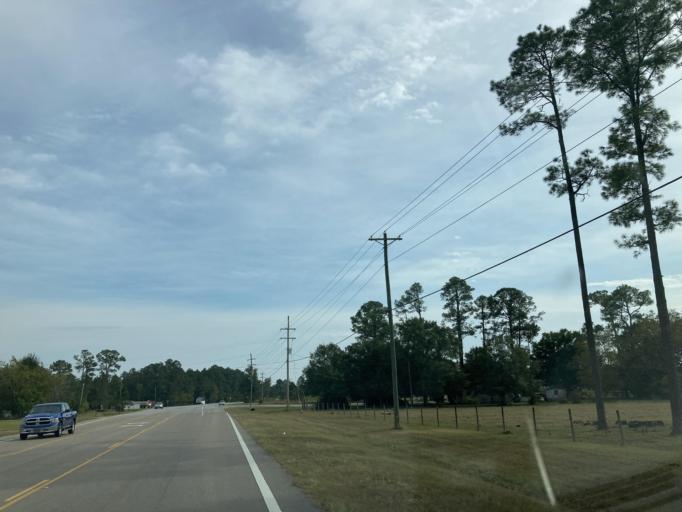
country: US
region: Mississippi
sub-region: Jackson County
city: Saint Martin
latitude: 30.4810
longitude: -88.8519
